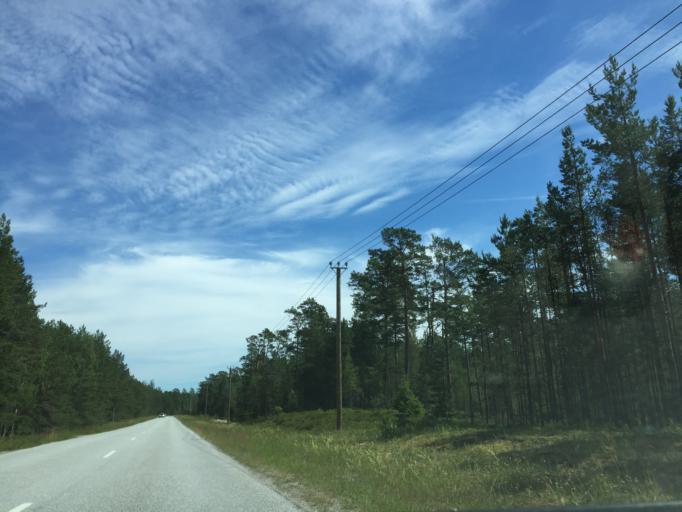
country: LV
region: Rojas
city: Roja
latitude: 57.5718
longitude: 22.6395
